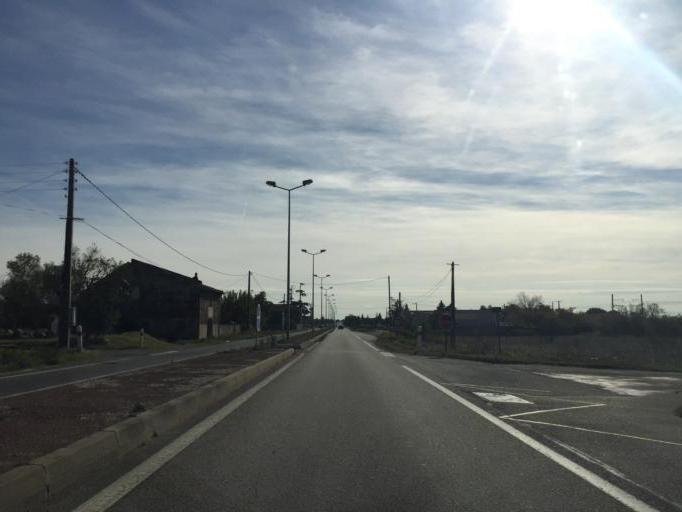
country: FR
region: Rhone-Alpes
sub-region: Departement de la Drome
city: Donzere
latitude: 44.4253
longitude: 4.7117
